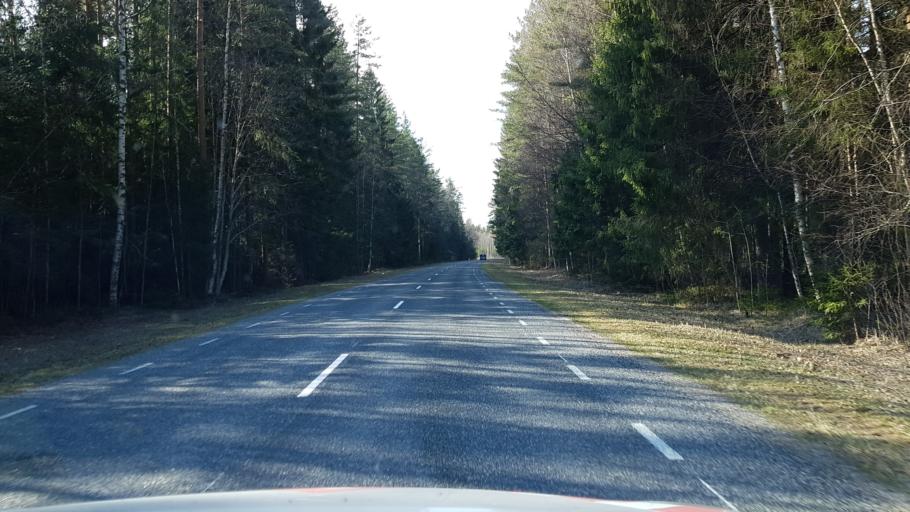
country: EE
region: Harju
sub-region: Loksa linn
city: Loksa
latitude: 59.5656
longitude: 25.9456
